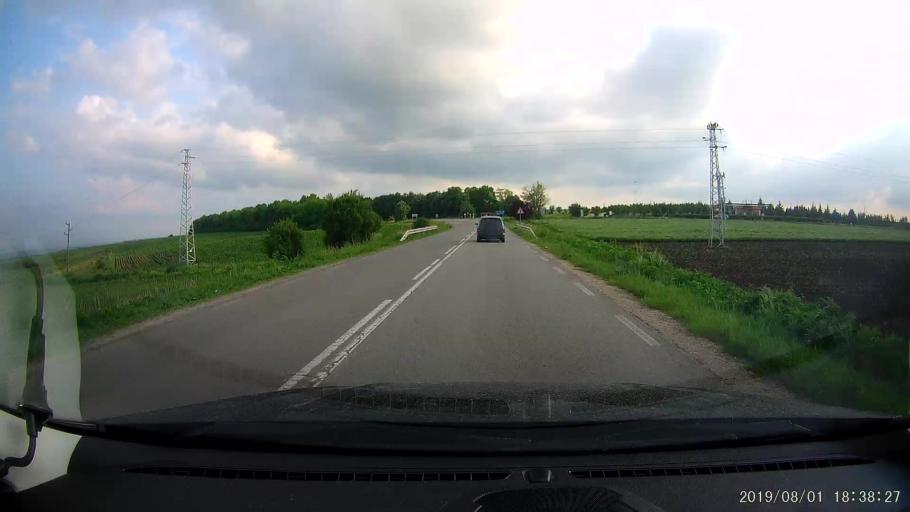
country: BG
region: Shumen
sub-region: Obshtina Khitrino
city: Gara Khitrino
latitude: 43.4018
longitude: 26.9167
